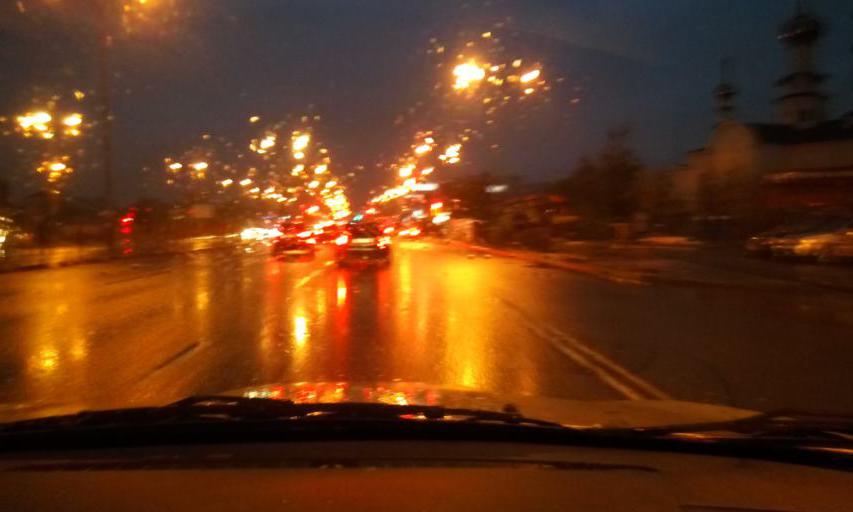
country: KZ
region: Astana Qalasy
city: Astana
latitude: 51.1769
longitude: 71.3922
